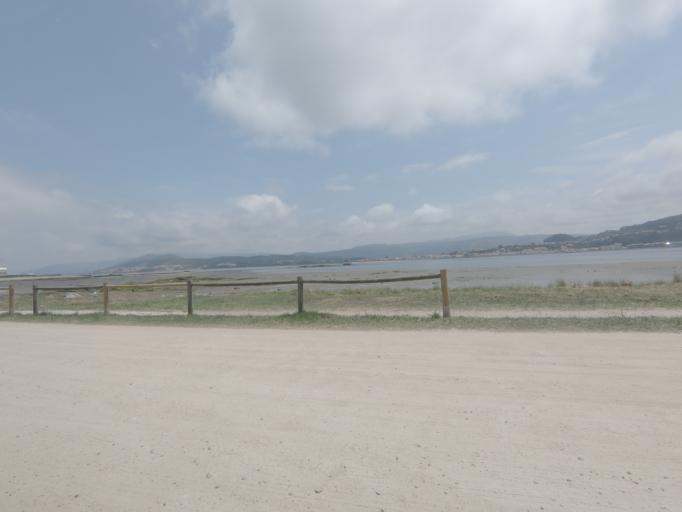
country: ES
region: Galicia
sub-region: Provincia de Pontevedra
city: A Guarda
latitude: 41.8815
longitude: -8.8595
